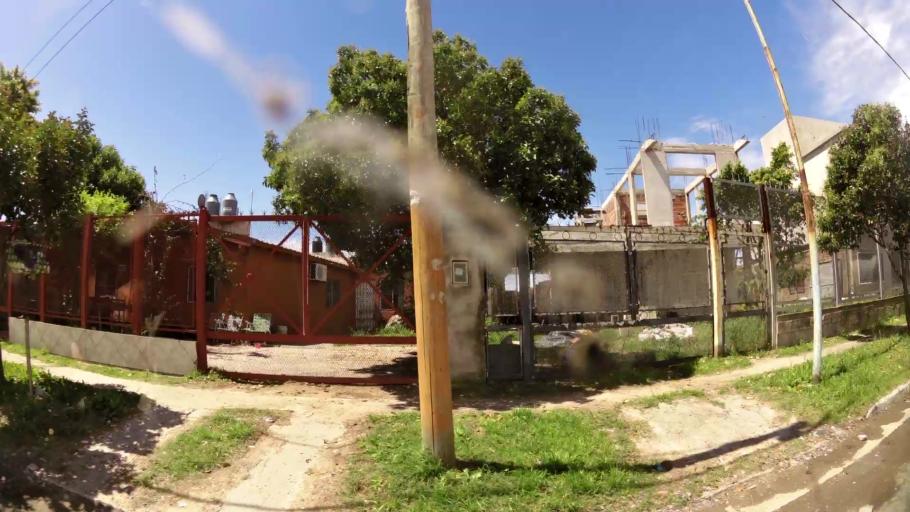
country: AR
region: Buenos Aires
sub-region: Partido de Quilmes
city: Quilmes
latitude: -34.7448
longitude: -58.3123
